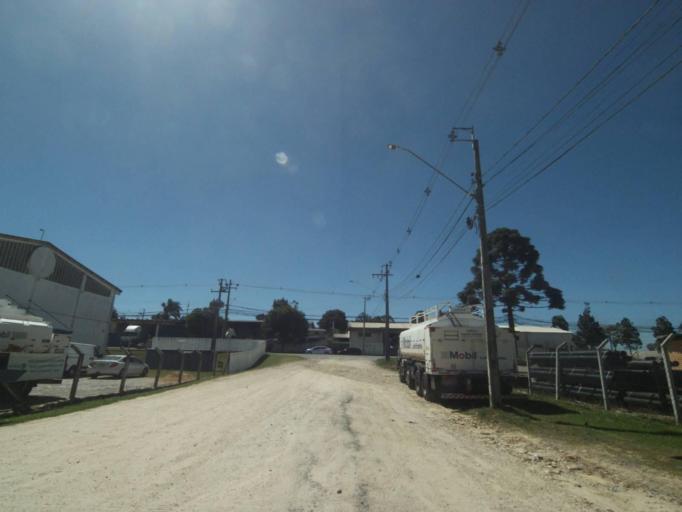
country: BR
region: Parana
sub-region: Curitiba
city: Curitiba
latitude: -25.4710
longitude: -49.3514
